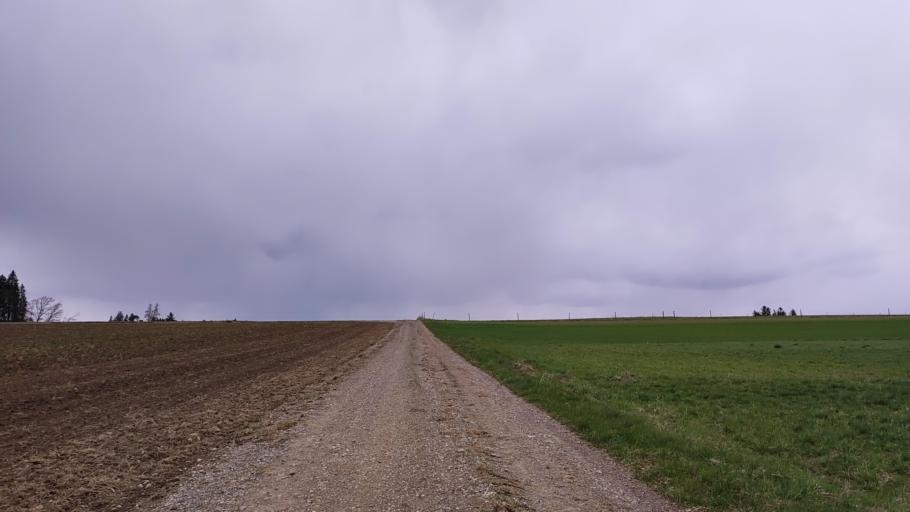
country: DE
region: Bavaria
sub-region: Swabia
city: Dinkelscherben
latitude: 48.3680
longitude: 10.5600
